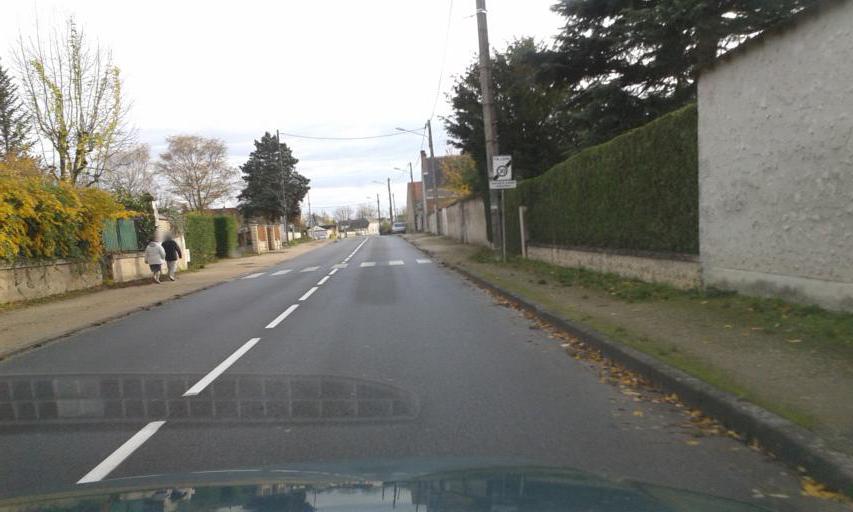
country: FR
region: Centre
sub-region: Departement du Loiret
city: Beaugency
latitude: 47.7965
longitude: 1.6264
